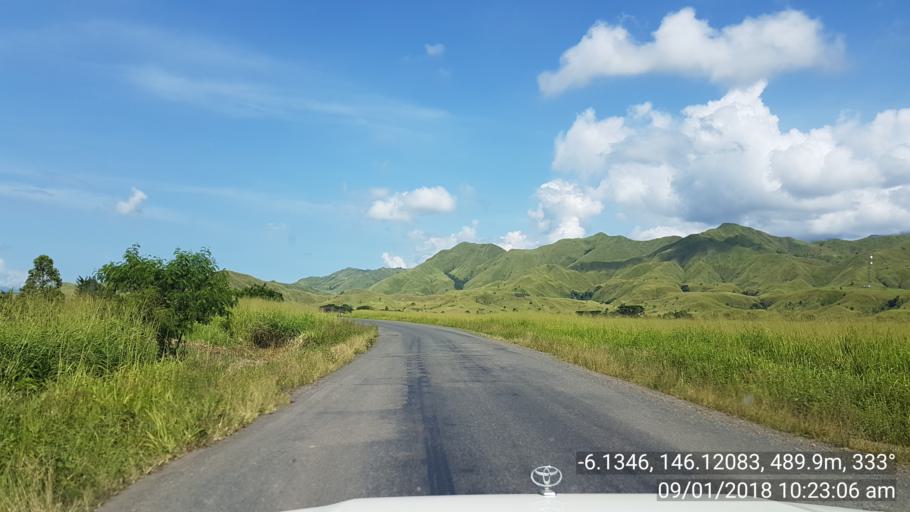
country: PG
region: Eastern Highlands
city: Kainantu
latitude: -6.1351
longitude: 146.1212
